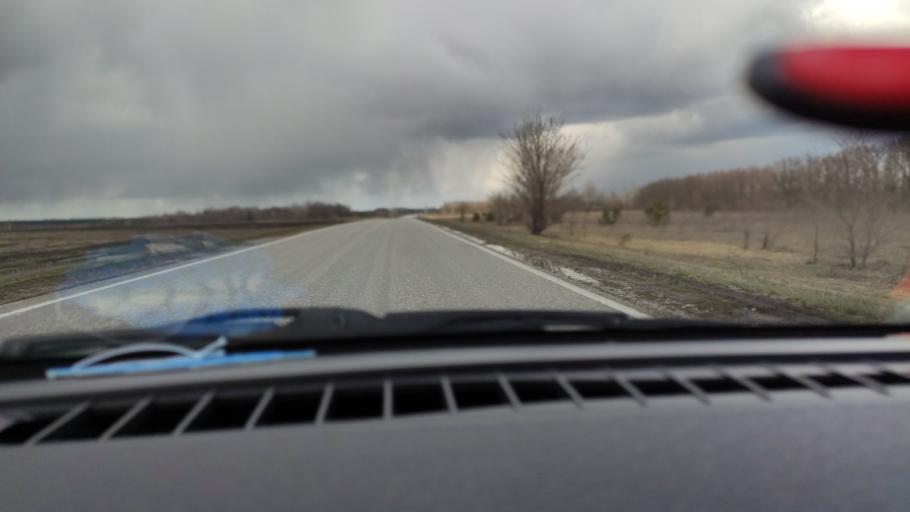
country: RU
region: Samara
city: Povolzhskiy
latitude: 53.7934
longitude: 49.7428
